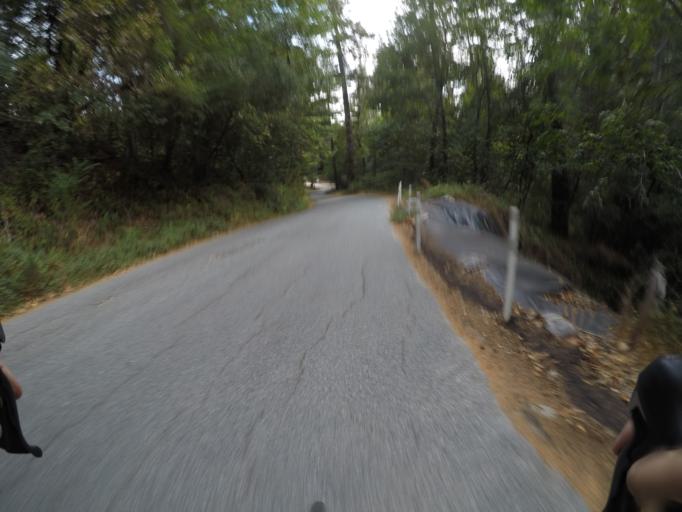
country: US
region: California
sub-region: Santa Cruz County
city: Scotts Valley
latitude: 37.0825
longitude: -122.0102
